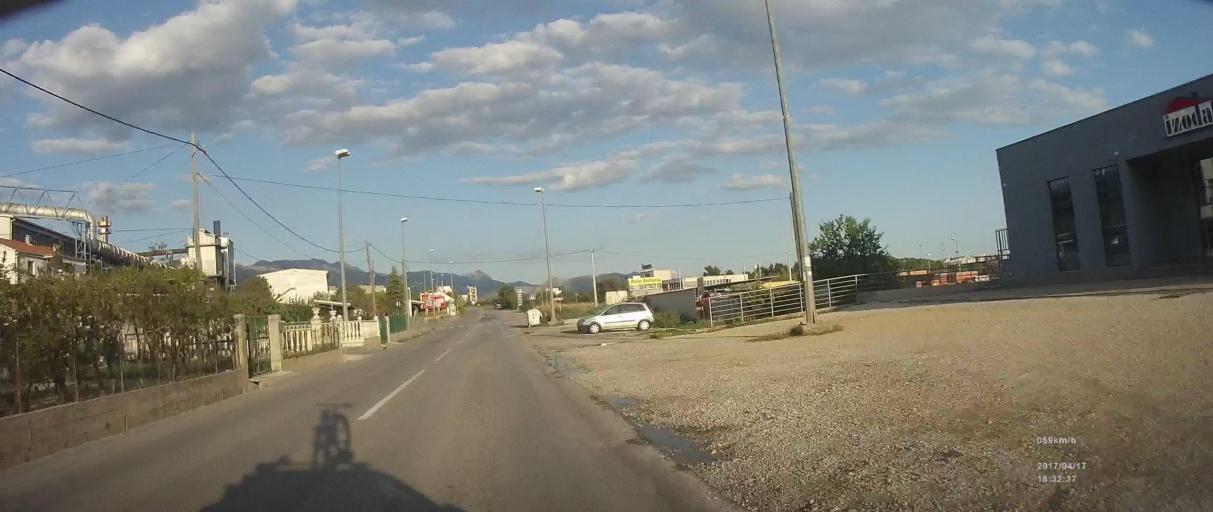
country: HR
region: Splitsko-Dalmatinska
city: Vranjic
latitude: 43.5419
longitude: 16.4482
